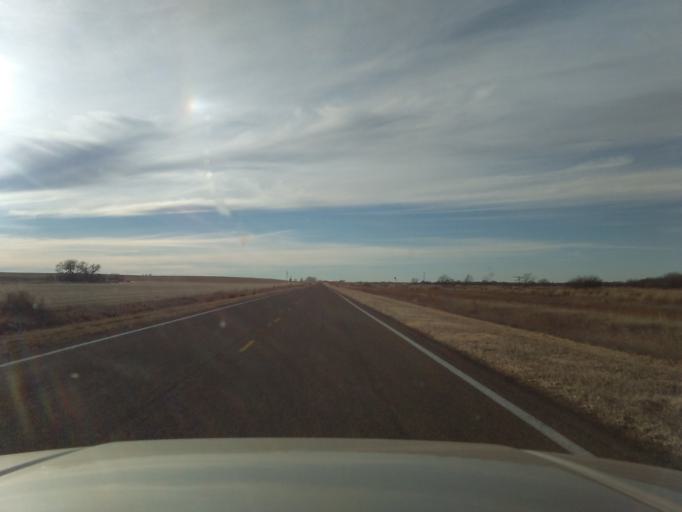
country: US
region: Kansas
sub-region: Norton County
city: Norton
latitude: 39.7540
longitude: -100.1287
